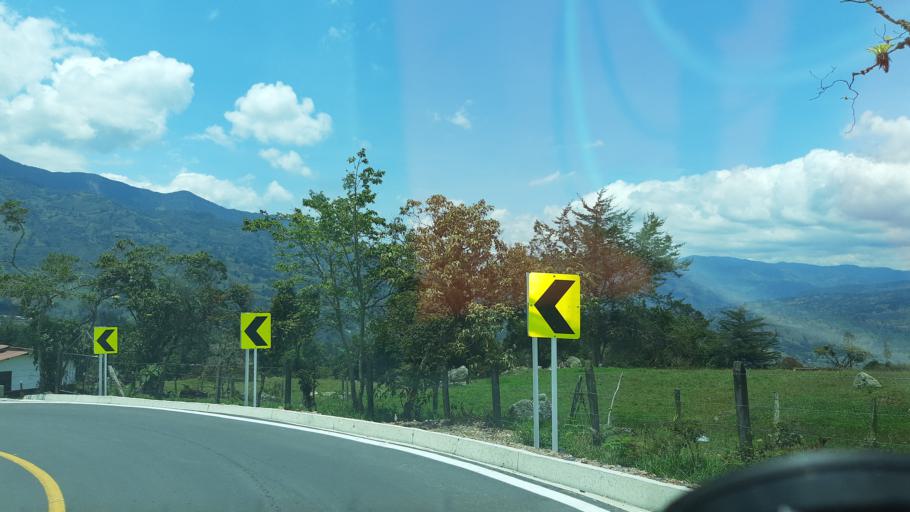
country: CO
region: Boyaca
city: Chinavita
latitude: 5.1365
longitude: -73.3926
